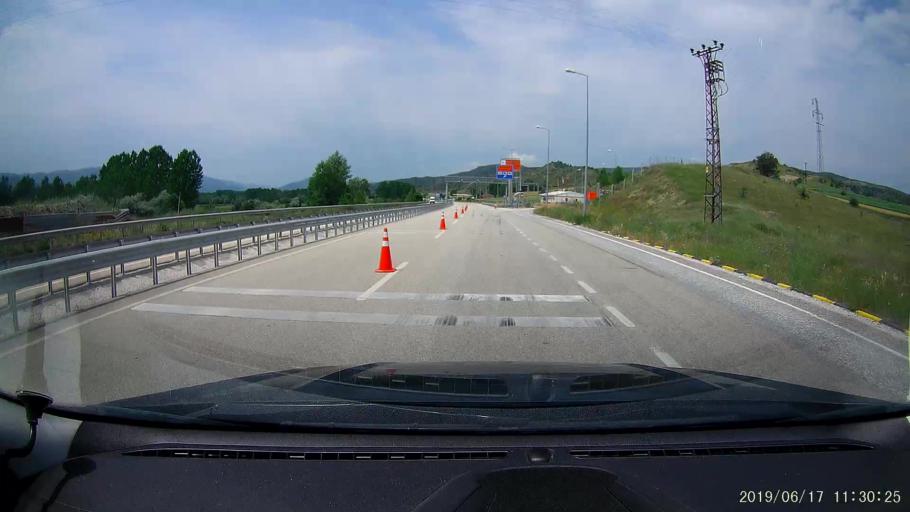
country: TR
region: Cankiri
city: Ilgaz
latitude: 40.9068
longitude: 33.5788
